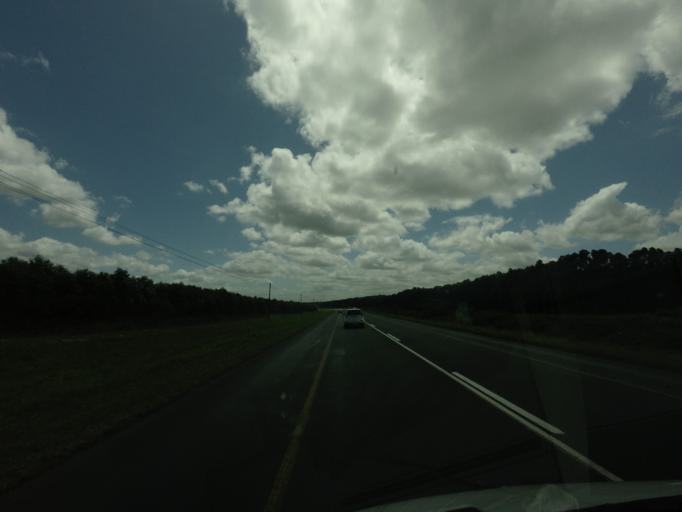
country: ZA
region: KwaZulu-Natal
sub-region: uThungulu District Municipality
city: KwaMbonambi
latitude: -28.5699
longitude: 32.1108
